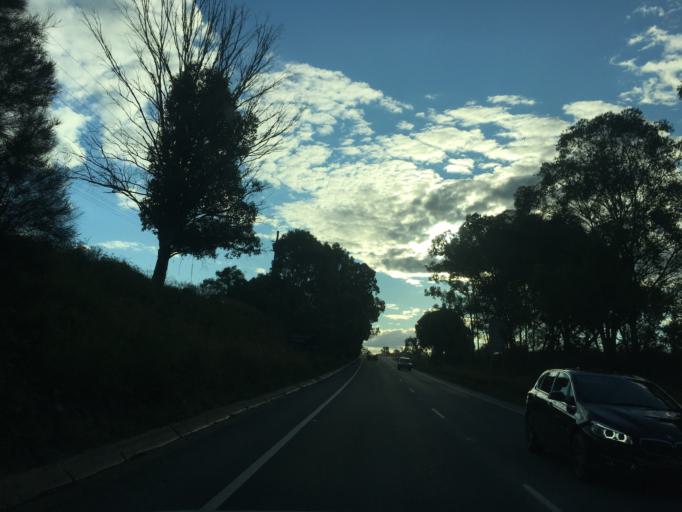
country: AU
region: New South Wales
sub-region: Liverpool
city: Bringelly
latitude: -33.8756
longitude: 150.7667
